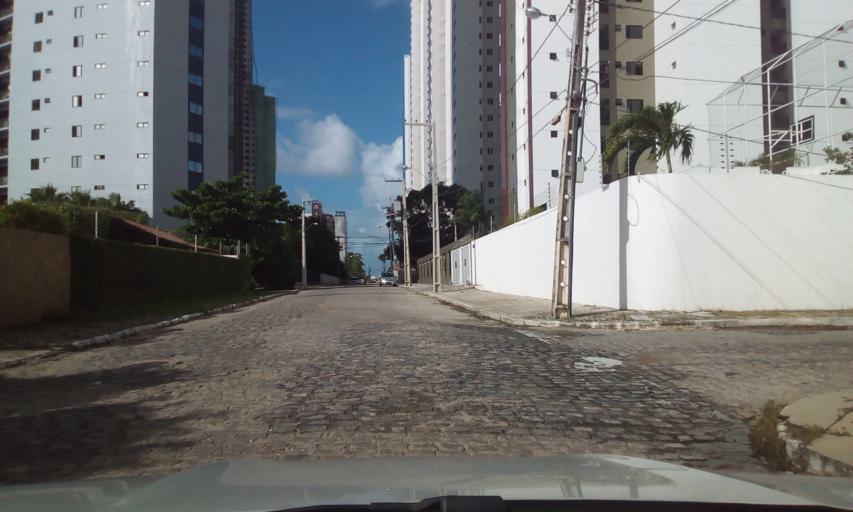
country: BR
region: Paraiba
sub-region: Joao Pessoa
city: Joao Pessoa
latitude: -7.1320
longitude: -34.8303
